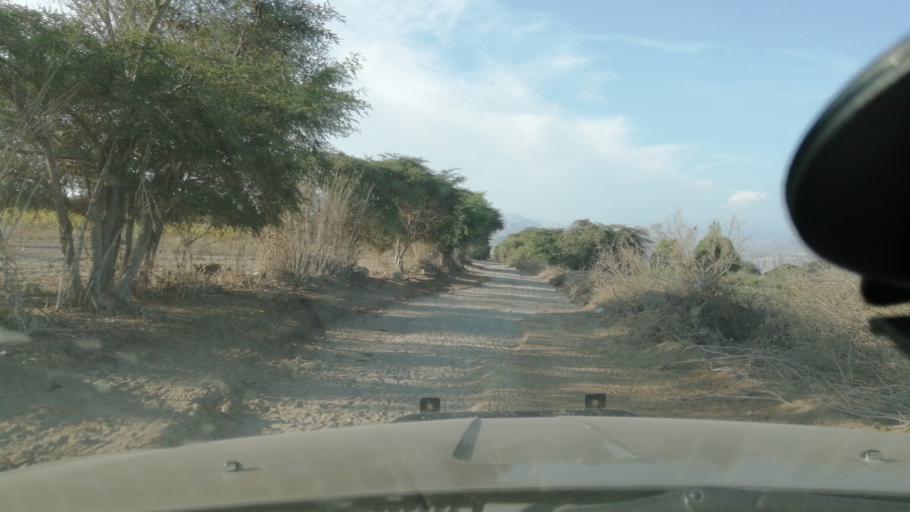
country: PE
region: Ica
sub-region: Provincia de Chincha
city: San Pedro
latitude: -13.3453
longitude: -76.1605
